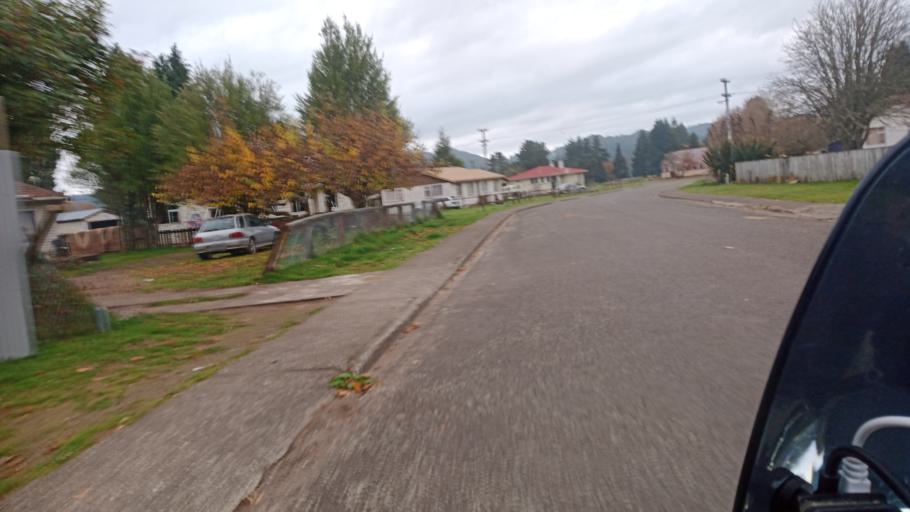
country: NZ
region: Bay of Plenty
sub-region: Whakatane District
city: Murupara
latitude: -38.6430
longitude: 176.7328
